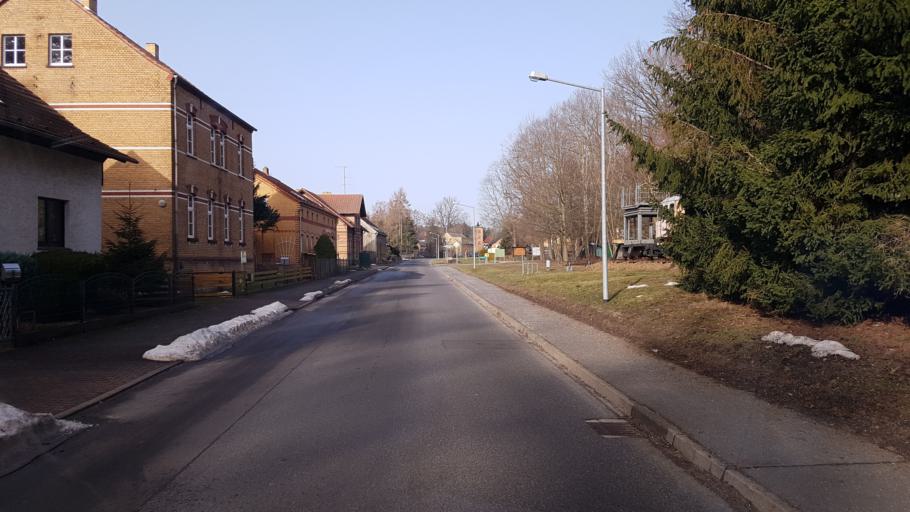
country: DE
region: Brandenburg
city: Schipkau
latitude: 51.5235
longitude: 13.8321
